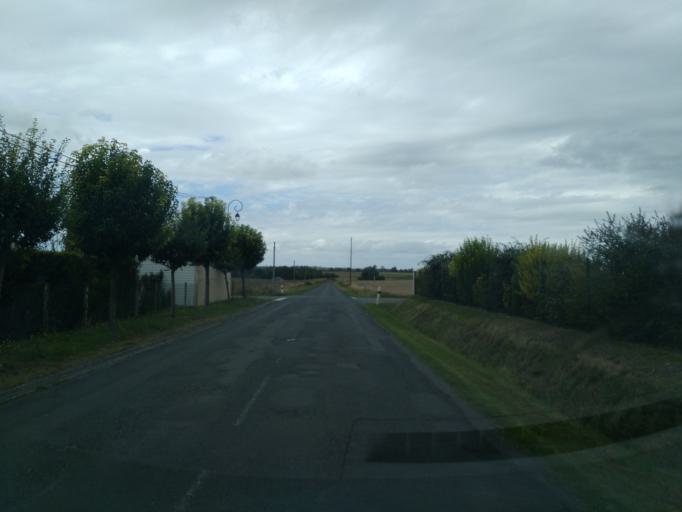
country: FR
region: Poitou-Charentes
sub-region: Departement de la Charente-Maritime
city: Pons
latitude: 45.6007
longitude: -0.5147
